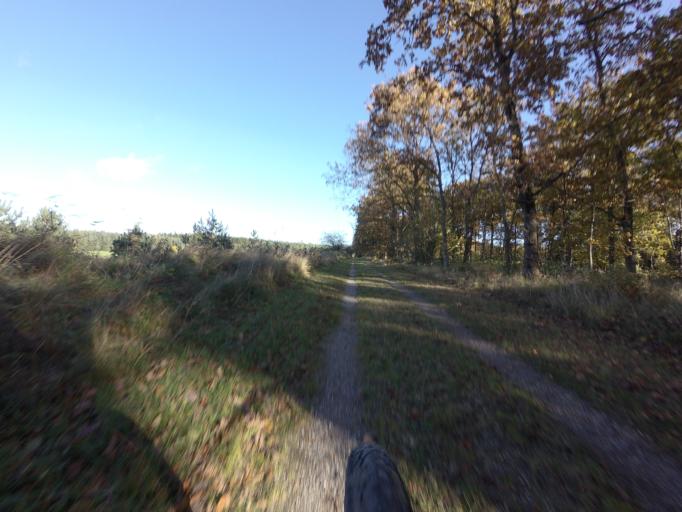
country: DK
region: Central Jutland
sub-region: Syddjurs Kommune
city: Ryomgard
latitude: 56.4254
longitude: 10.5967
